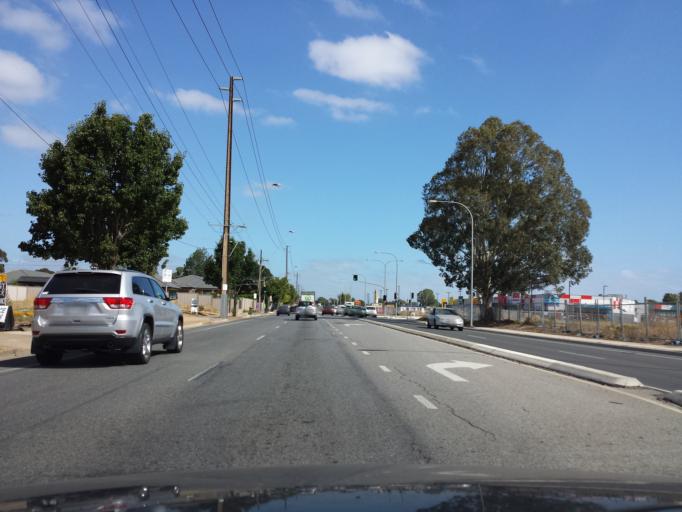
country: AU
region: South Australia
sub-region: Prospect
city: Prospect
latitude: -34.8701
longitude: 138.5838
